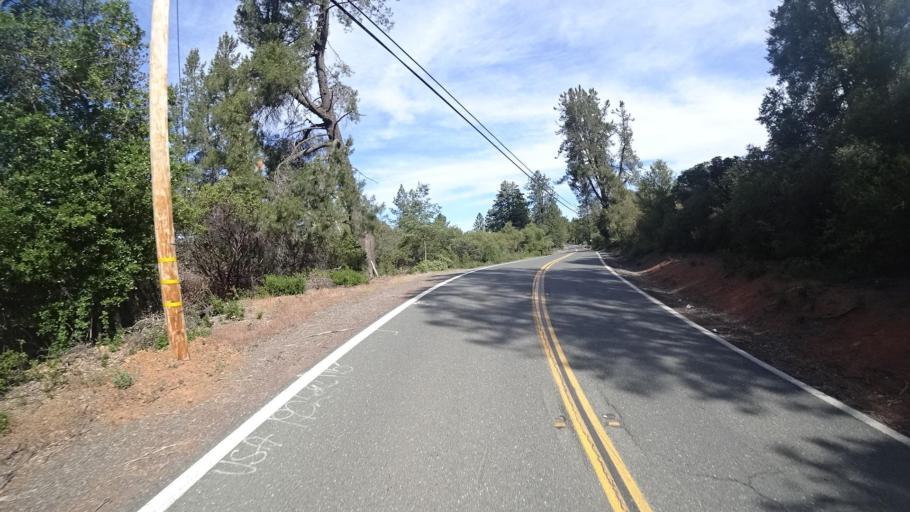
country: US
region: California
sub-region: Lake County
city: Soda Bay
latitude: 38.9083
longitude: -122.7652
